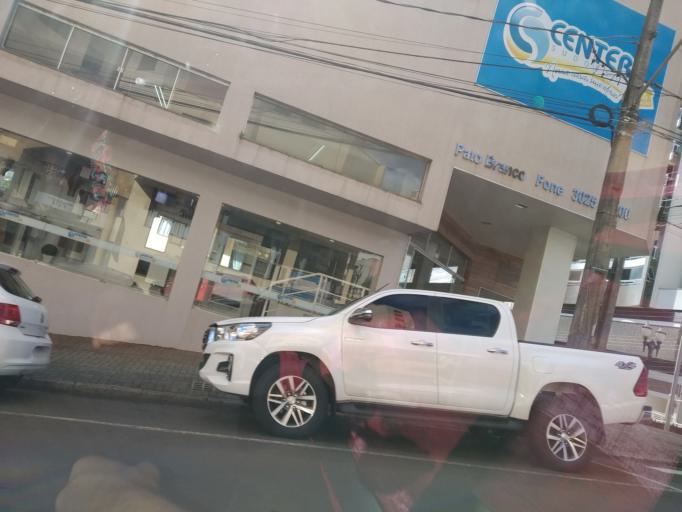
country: BR
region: Parana
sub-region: Pato Branco
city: Pato Branco
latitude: -26.2301
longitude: -52.6719
